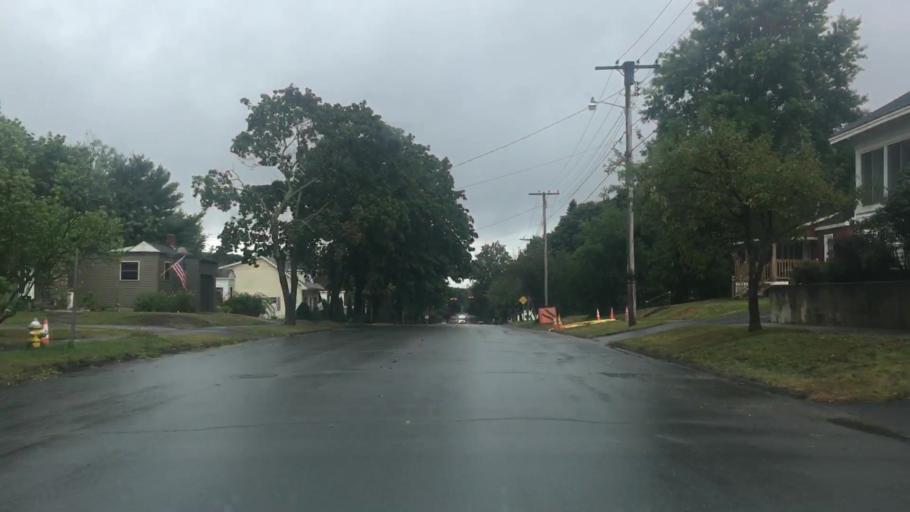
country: US
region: Maine
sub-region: Penobscot County
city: Brewer
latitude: 44.8156
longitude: -68.7600
